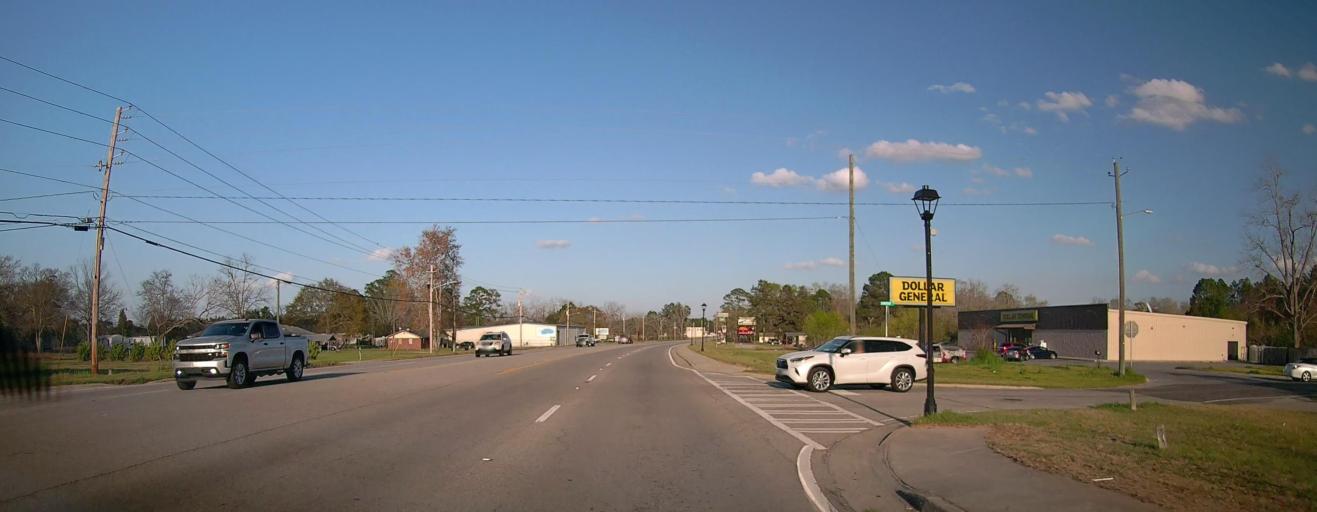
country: US
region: Georgia
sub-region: Evans County
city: Claxton
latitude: 32.1594
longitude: -81.9315
